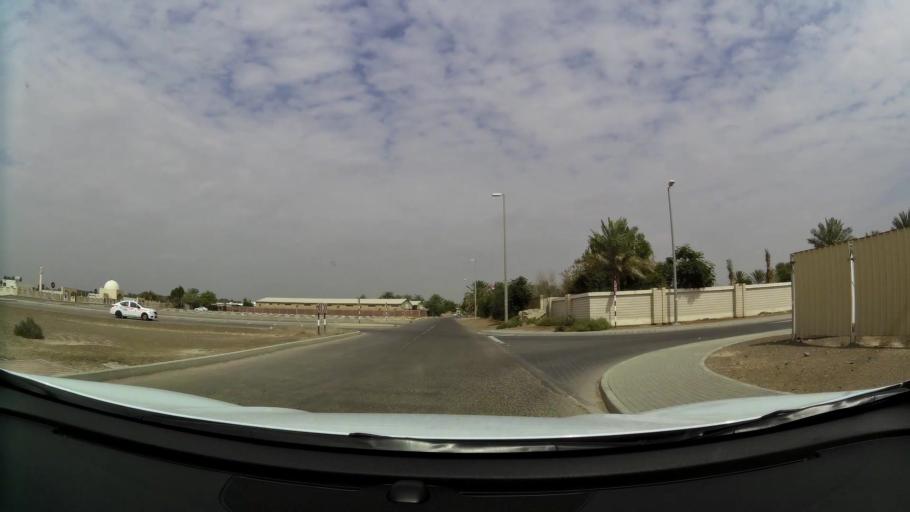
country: OM
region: Al Buraimi
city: Al Buraymi
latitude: 24.2136
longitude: 55.7945
